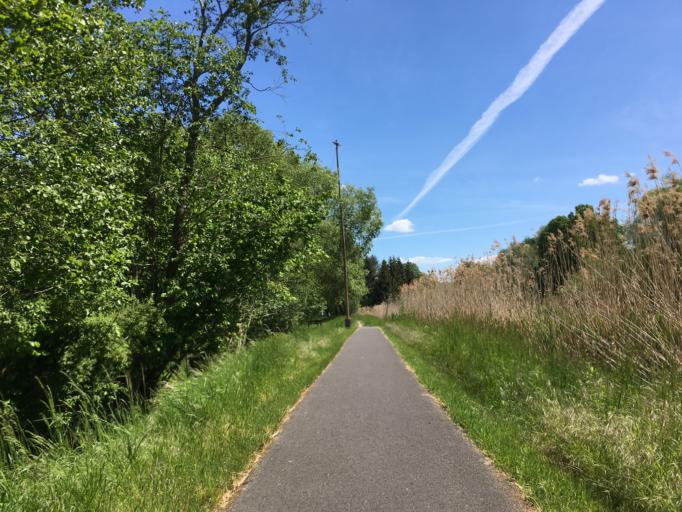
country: DE
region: Brandenburg
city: Eberswalde
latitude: 52.8491
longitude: 13.8529
